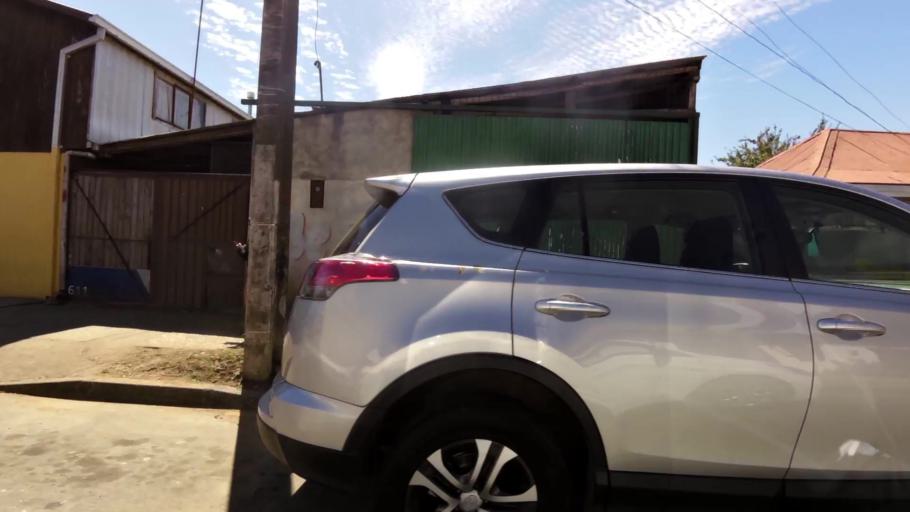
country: CL
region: Biobio
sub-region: Provincia de Concepcion
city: Penco
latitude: -36.7385
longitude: -72.9913
